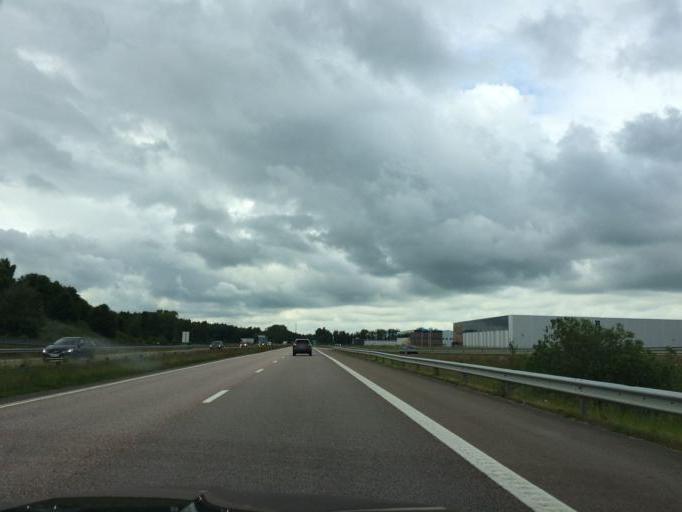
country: SE
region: Skane
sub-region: Helsingborg
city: Odakra
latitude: 56.0650
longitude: 12.7813
